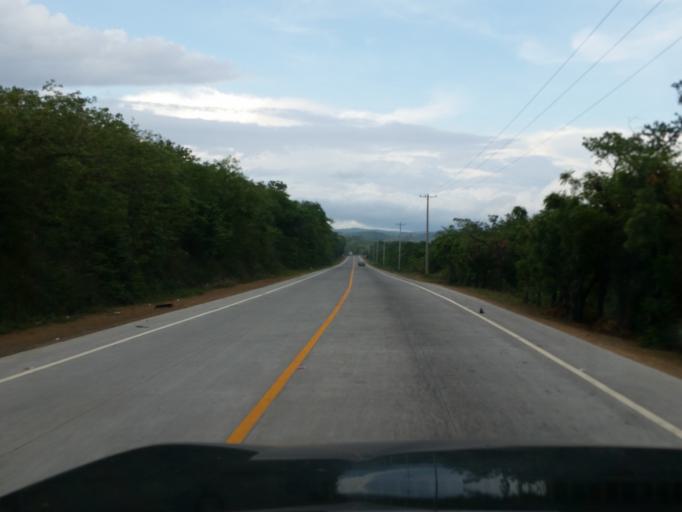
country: NI
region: Managua
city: Carlos Fonseca Amador
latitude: 12.0621
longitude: -86.4580
